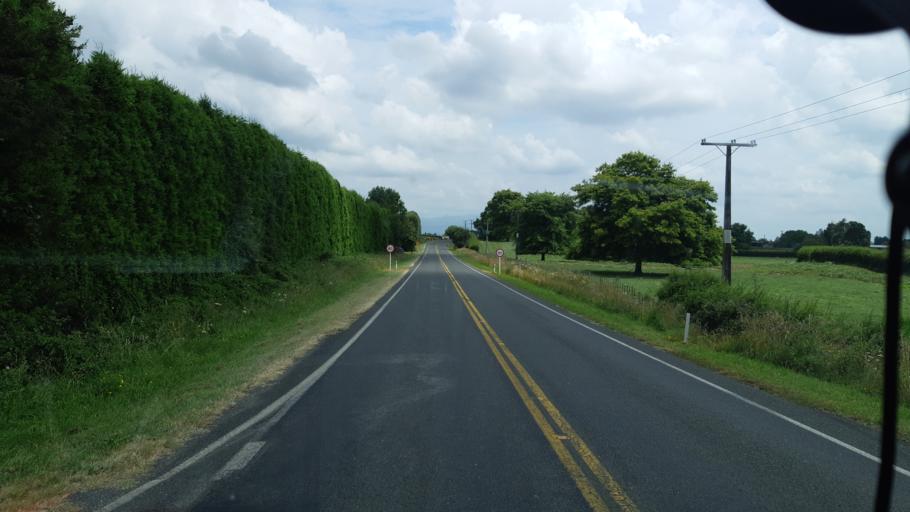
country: NZ
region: Waikato
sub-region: Waipa District
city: Cambridge
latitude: -38.0507
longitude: 175.3774
